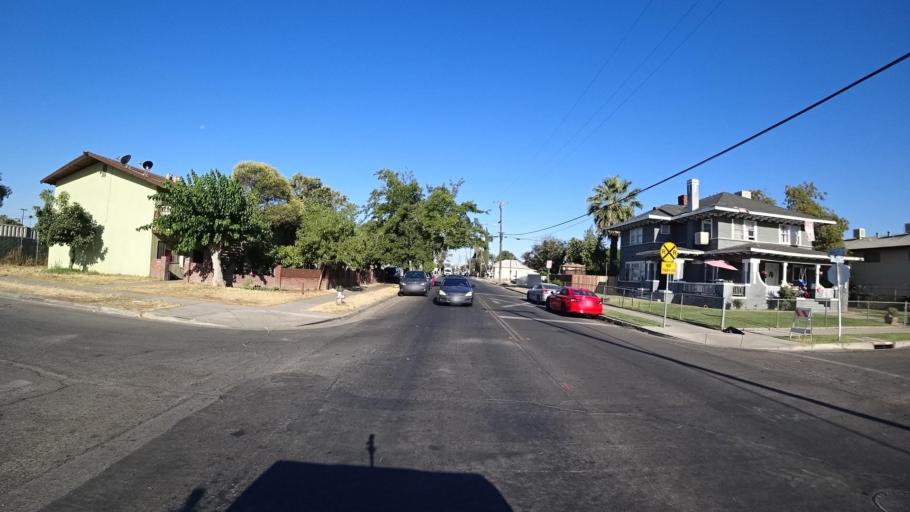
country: US
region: California
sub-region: Fresno County
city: Fresno
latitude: 36.7468
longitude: -119.7861
